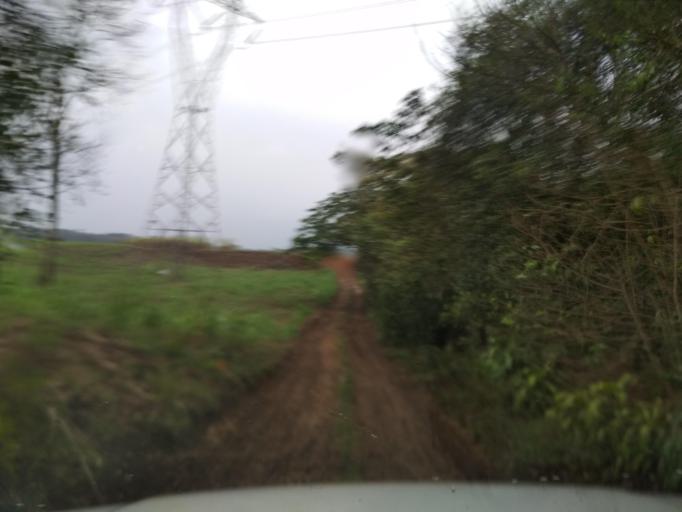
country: MX
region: Veracruz
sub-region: Cordoba
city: Fredepo
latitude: 18.8706
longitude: -96.9681
